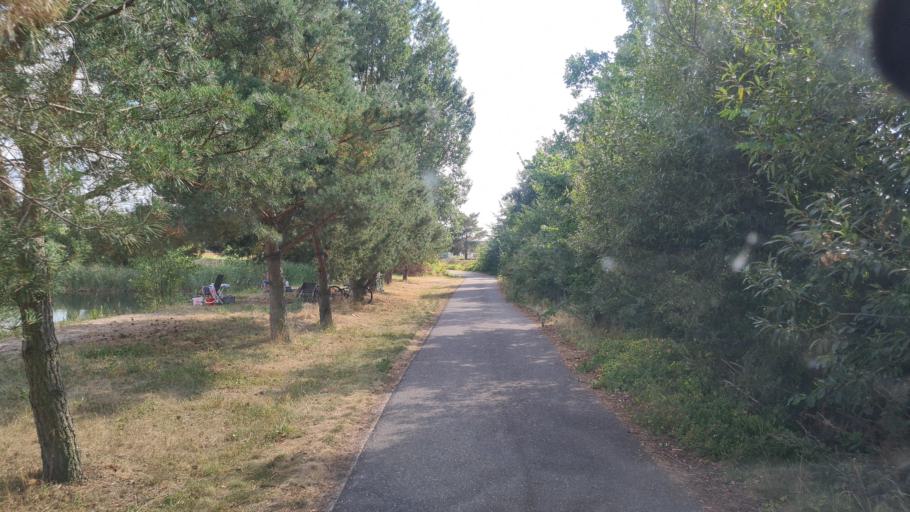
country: DE
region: Saxony-Anhalt
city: Elster
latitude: 51.8387
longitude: 12.8096
